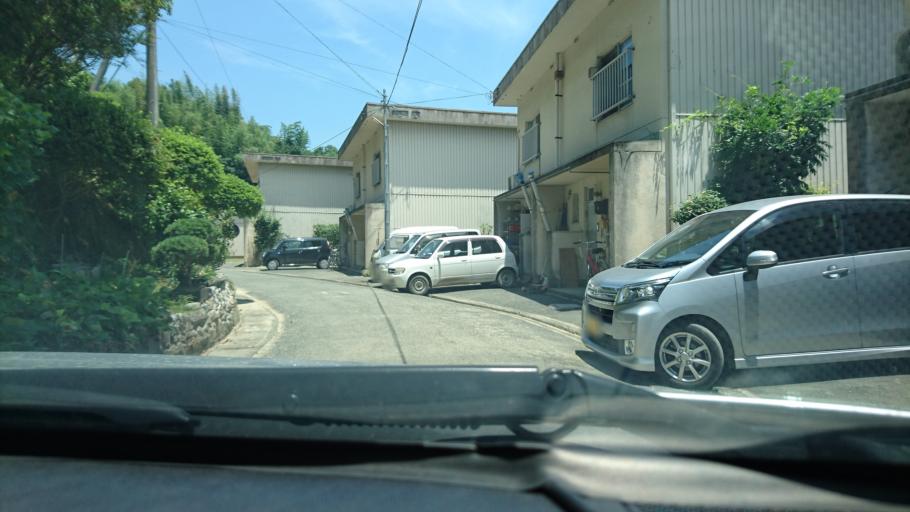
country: JP
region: Ehime
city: Ozu
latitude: 33.5099
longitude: 132.5314
